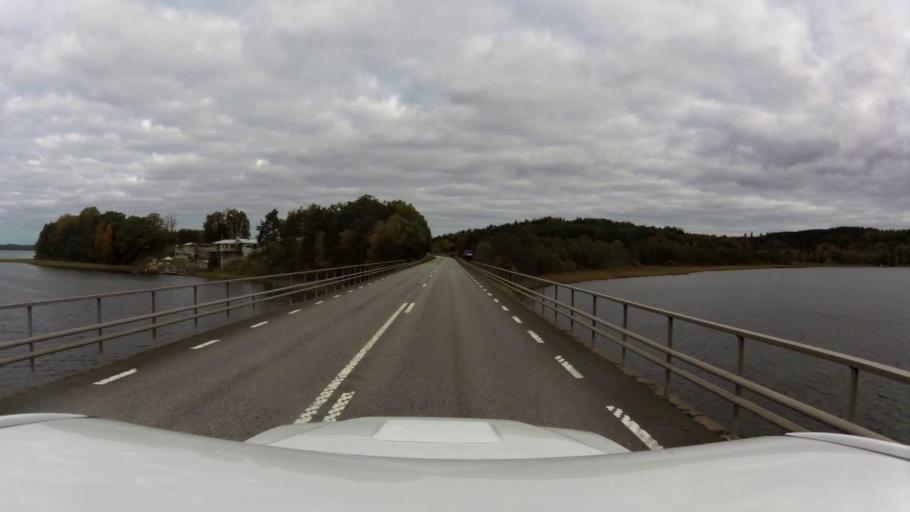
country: SE
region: OEstergoetland
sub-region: Kinda Kommun
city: Rimforsa
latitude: 58.1689
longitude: 15.6775
